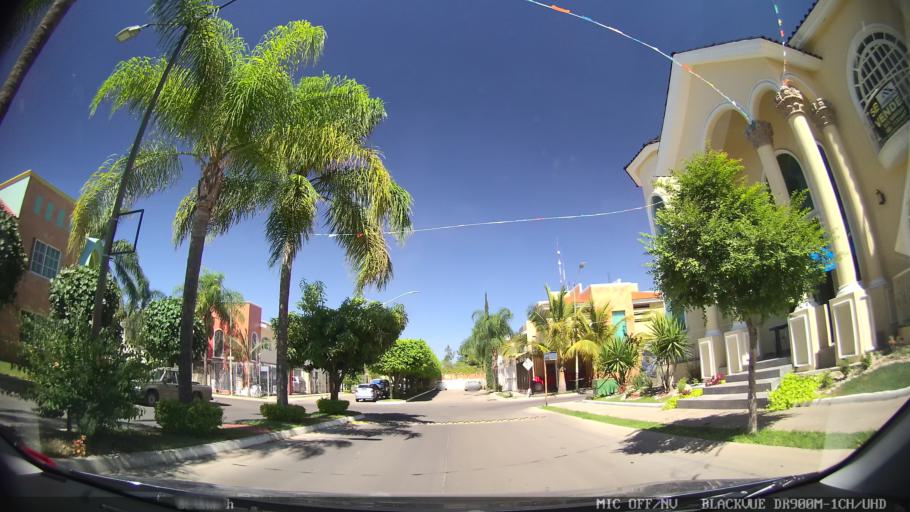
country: MX
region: Jalisco
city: Tlaquepaque
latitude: 20.6467
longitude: -103.2824
